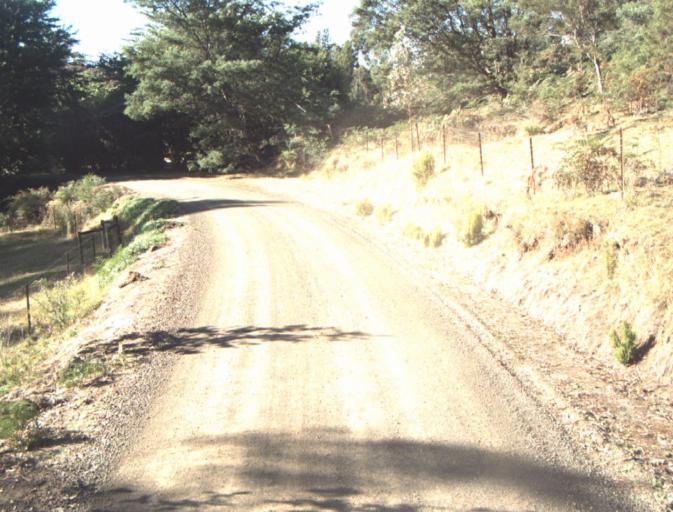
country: AU
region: Tasmania
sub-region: Launceston
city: Mayfield
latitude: -41.2994
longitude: 147.1975
